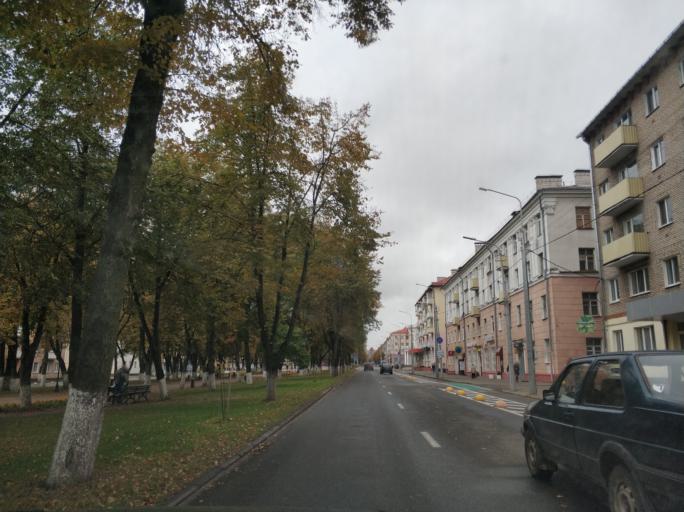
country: BY
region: Vitebsk
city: Polatsk
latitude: 55.4844
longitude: 28.7814
